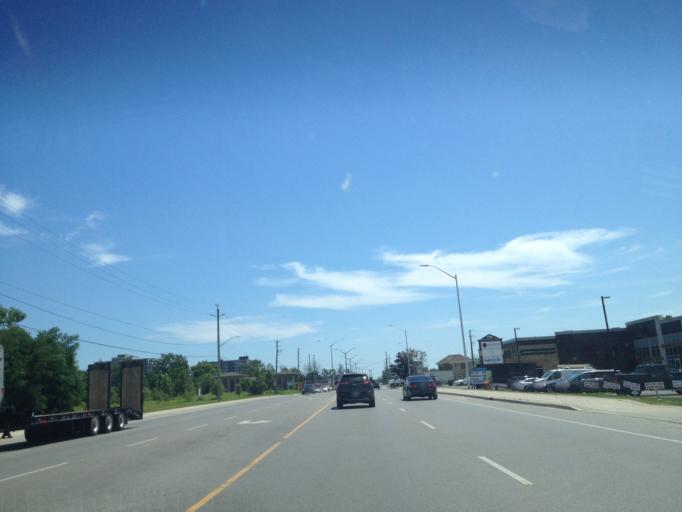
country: CA
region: Ontario
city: London
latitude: 43.0020
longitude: -81.3337
